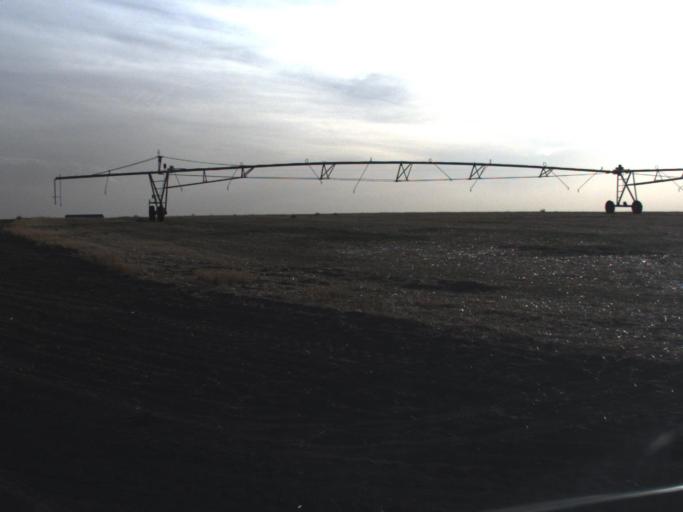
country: US
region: Washington
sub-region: Adams County
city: Ritzville
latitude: 47.3009
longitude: -118.6902
